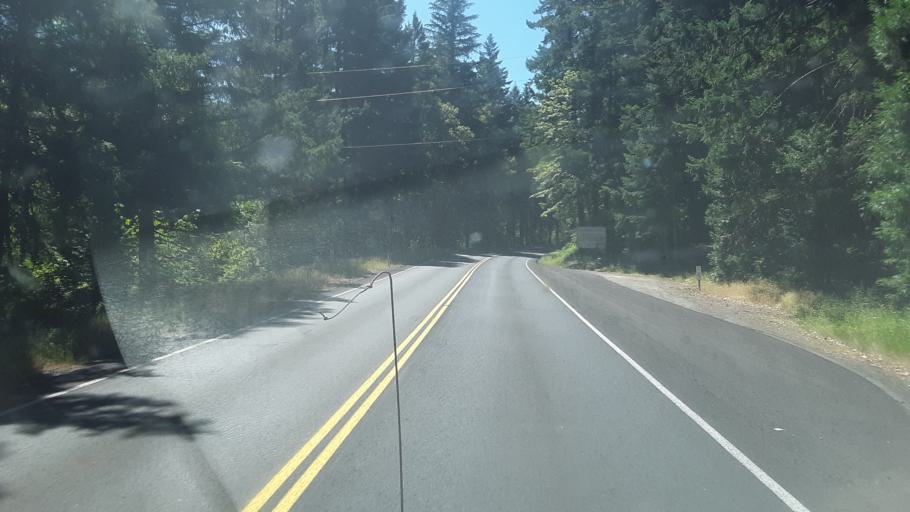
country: US
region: Oregon
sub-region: Josephine County
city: Cave Junction
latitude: 41.9919
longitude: -123.7188
